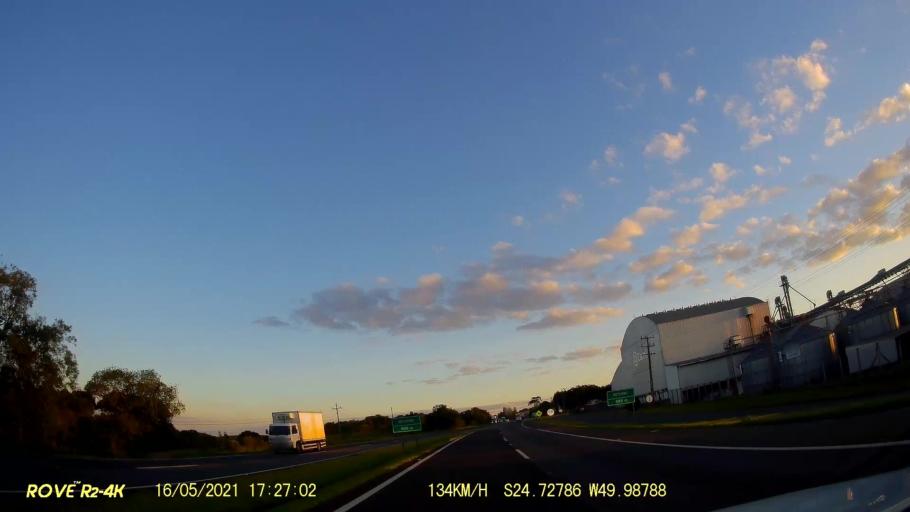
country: BR
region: Parana
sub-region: Castro
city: Castro
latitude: -24.7284
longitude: -49.9881
